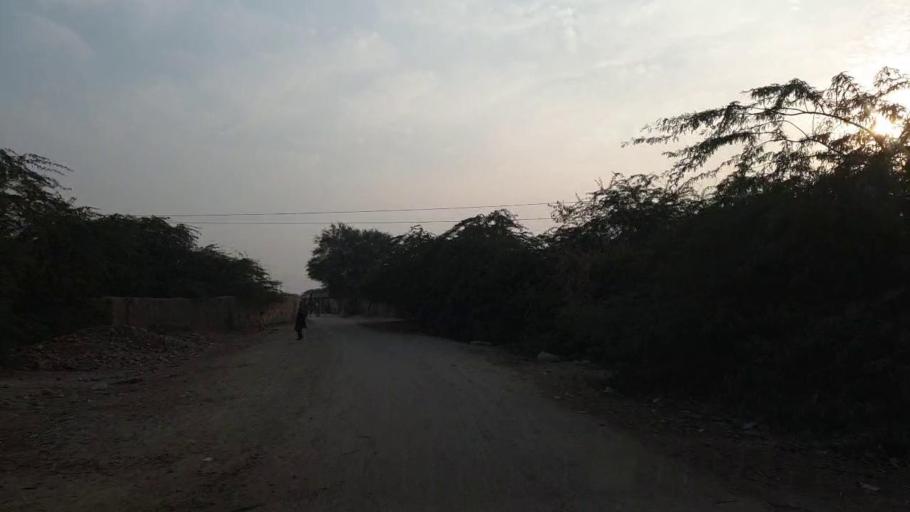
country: PK
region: Sindh
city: Sann
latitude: 26.1657
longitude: 68.0082
